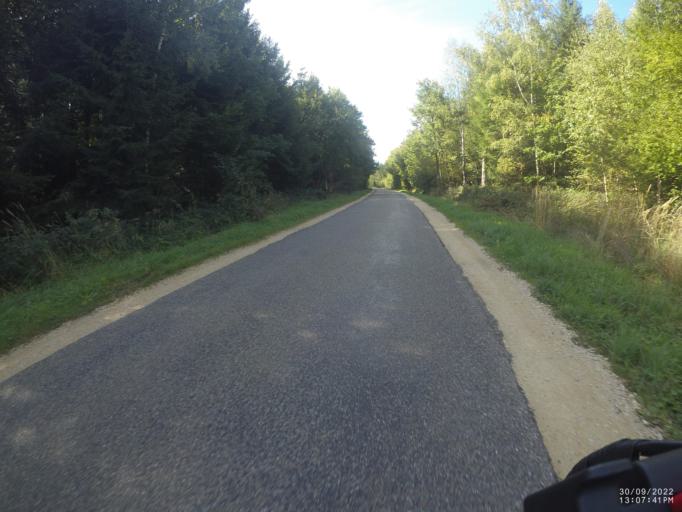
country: DE
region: Baden-Wuerttemberg
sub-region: Regierungsbezirk Stuttgart
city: Pluderhausen
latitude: 48.7803
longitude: 9.5858
